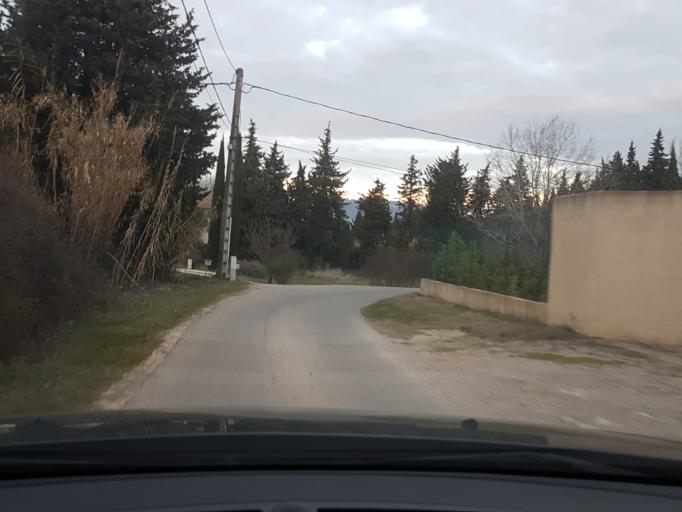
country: FR
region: Provence-Alpes-Cote d'Azur
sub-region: Departement du Vaucluse
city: Loriol-du-Comtat
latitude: 44.0891
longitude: 4.9970
